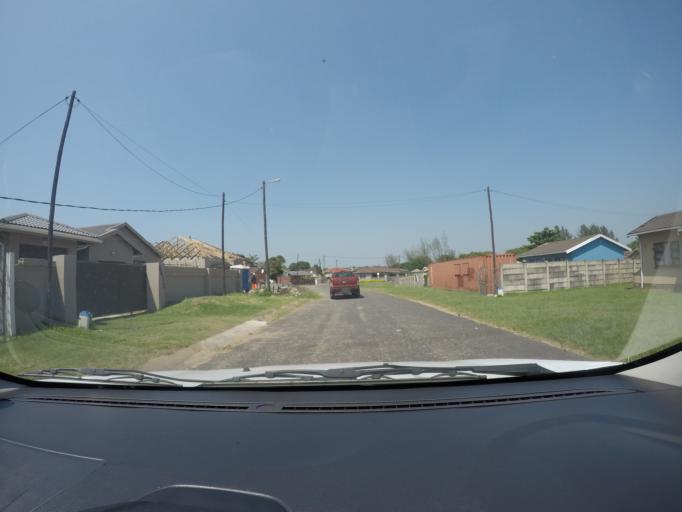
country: ZA
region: KwaZulu-Natal
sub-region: uThungulu District Municipality
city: eSikhawini
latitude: -28.8634
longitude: 31.9202
